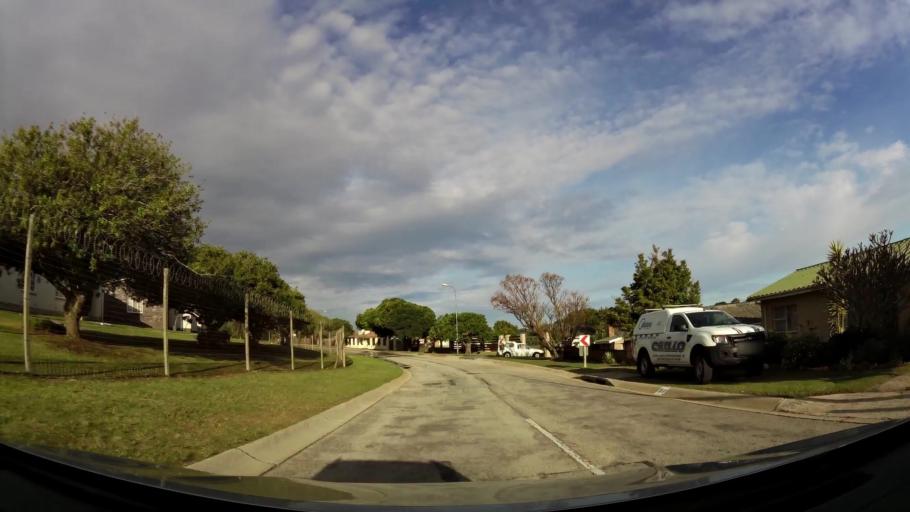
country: ZA
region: Eastern Cape
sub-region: Nelson Mandela Bay Metropolitan Municipality
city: Port Elizabeth
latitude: -33.9476
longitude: 25.4904
